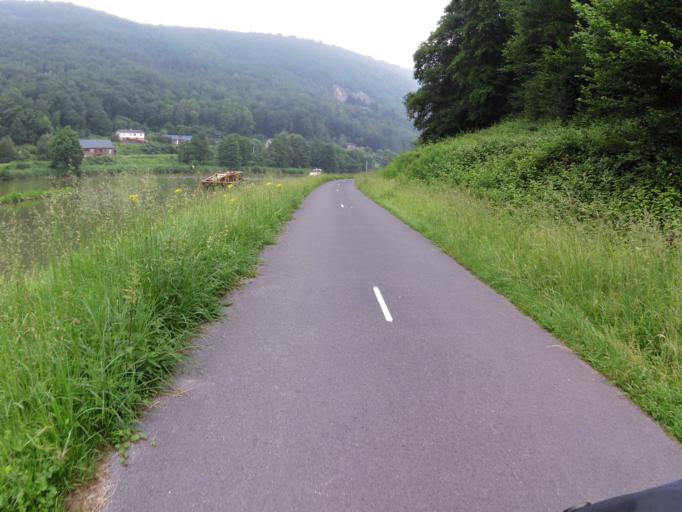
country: FR
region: Champagne-Ardenne
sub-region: Departement des Ardennes
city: Haybes
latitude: 50.0074
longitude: 4.6968
